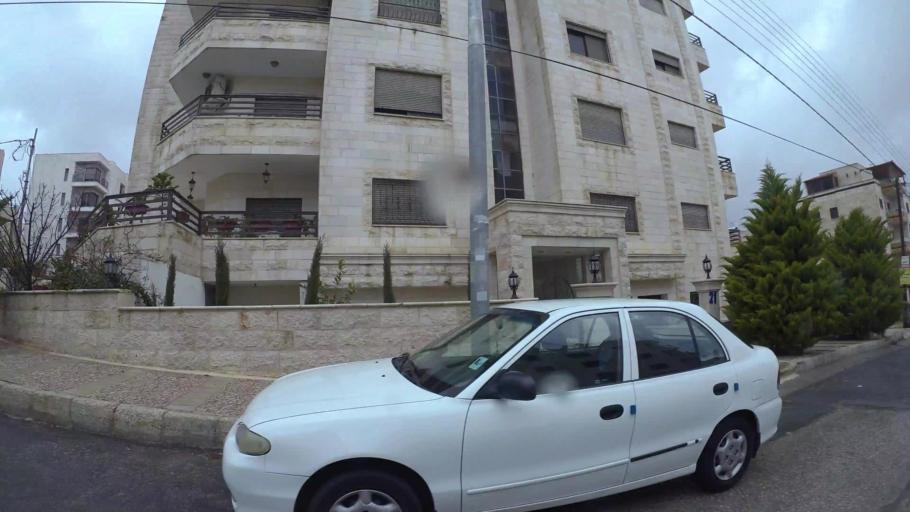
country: JO
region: Amman
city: Al Jubayhah
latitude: 32.0367
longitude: 35.8861
